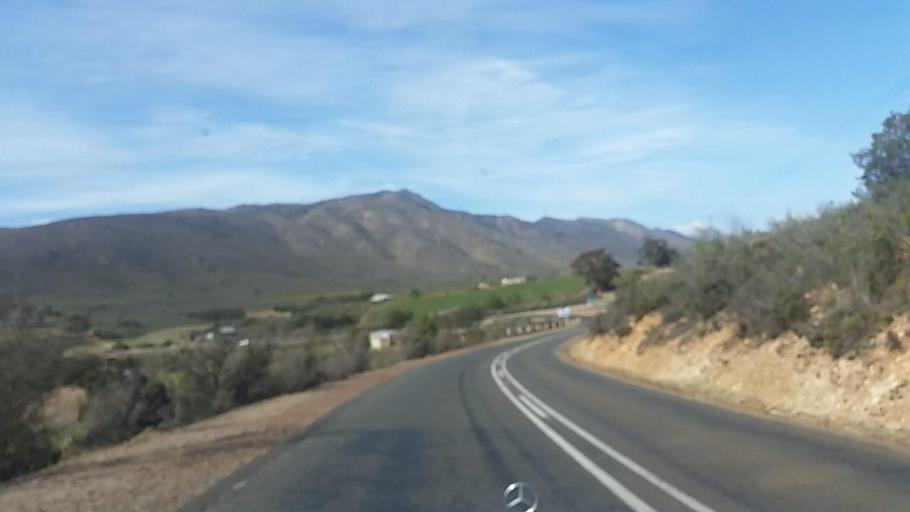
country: ZA
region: Western Cape
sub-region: Eden District Municipality
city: George
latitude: -33.8199
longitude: 22.3518
